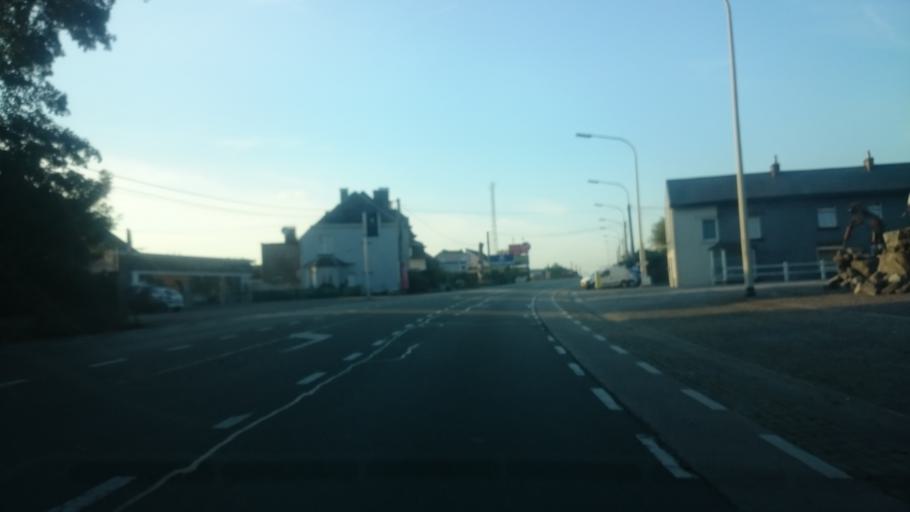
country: BE
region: Wallonia
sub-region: Province de Namur
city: Gembloux
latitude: 50.5751
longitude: 4.6898
